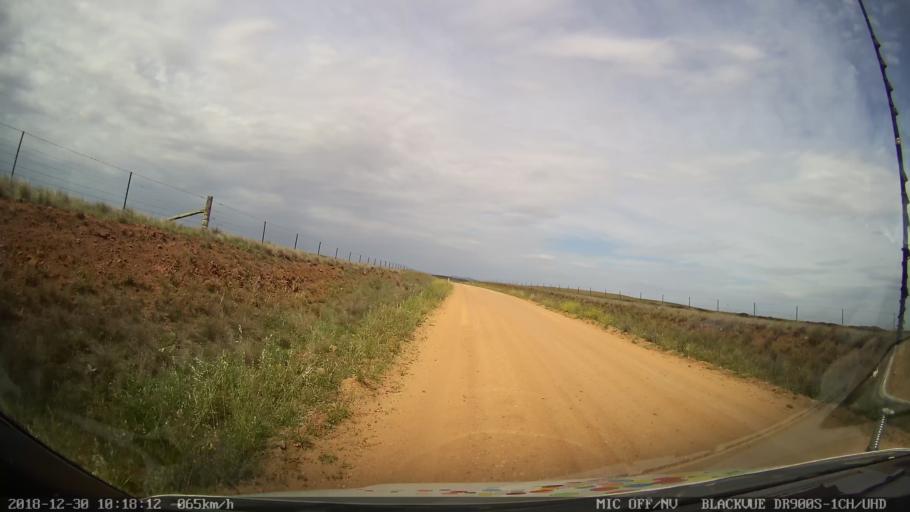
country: AU
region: New South Wales
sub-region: Snowy River
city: Berridale
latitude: -36.5510
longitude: 149.0115
